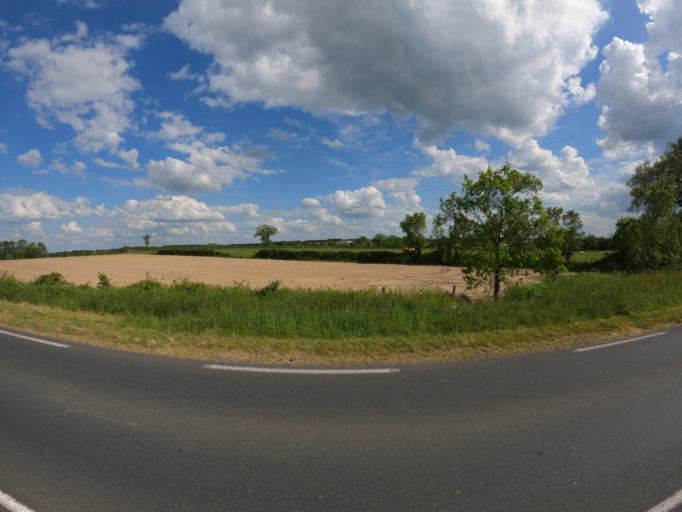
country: FR
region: Pays de la Loire
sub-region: Departement de Maine-et-Loire
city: Le Longeron
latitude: 47.0501
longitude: -1.0630
